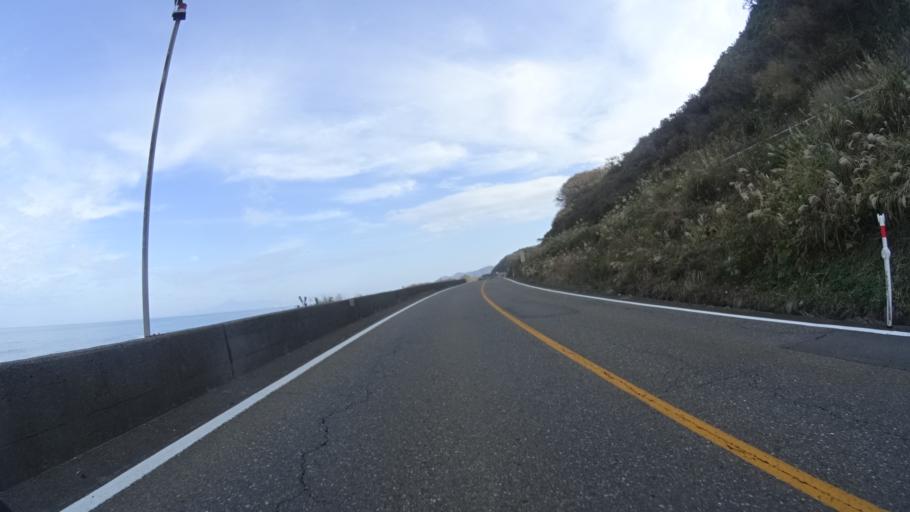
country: JP
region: Niigata
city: Joetsu
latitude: 37.1721
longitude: 138.1100
